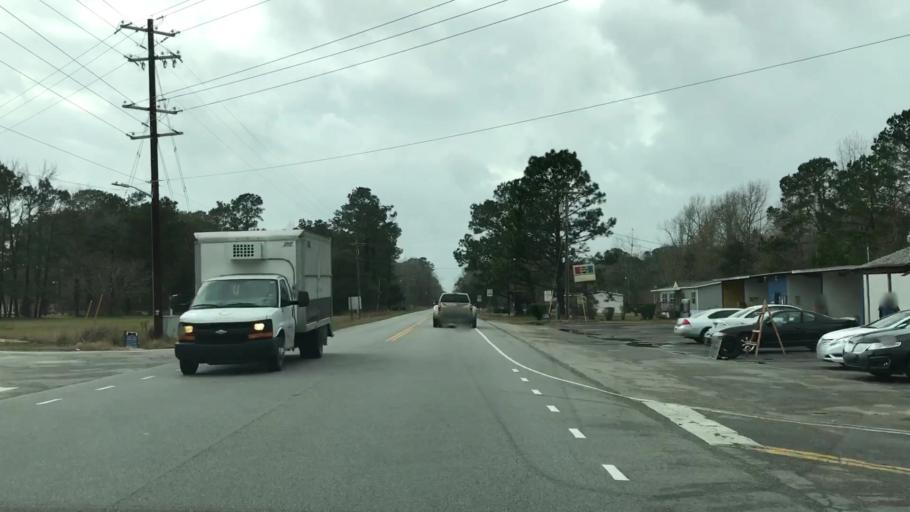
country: US
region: South Carolina
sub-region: Horry County
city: Socastee
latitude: 33.6911
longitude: -79.1176
